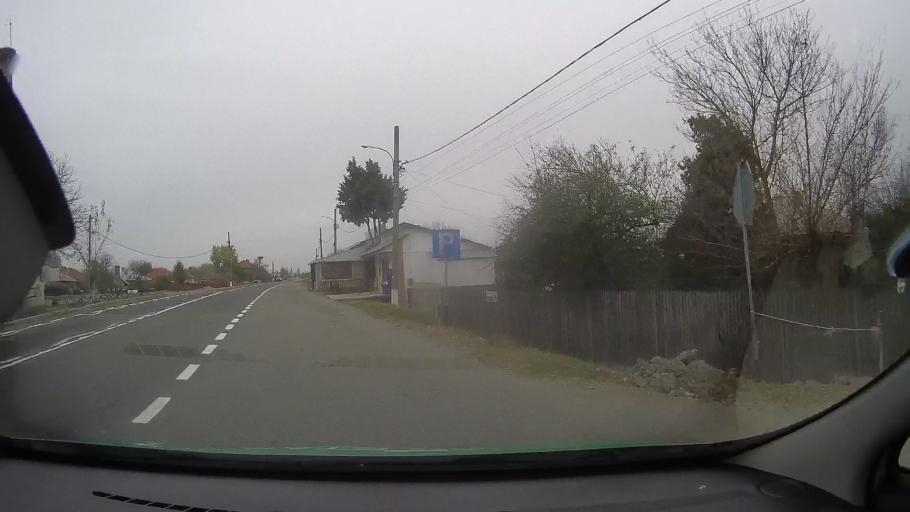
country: RO
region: Ialomita
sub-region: Comuna Giurgeni
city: Giurgeni
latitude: 44.7445
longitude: 27.8567
